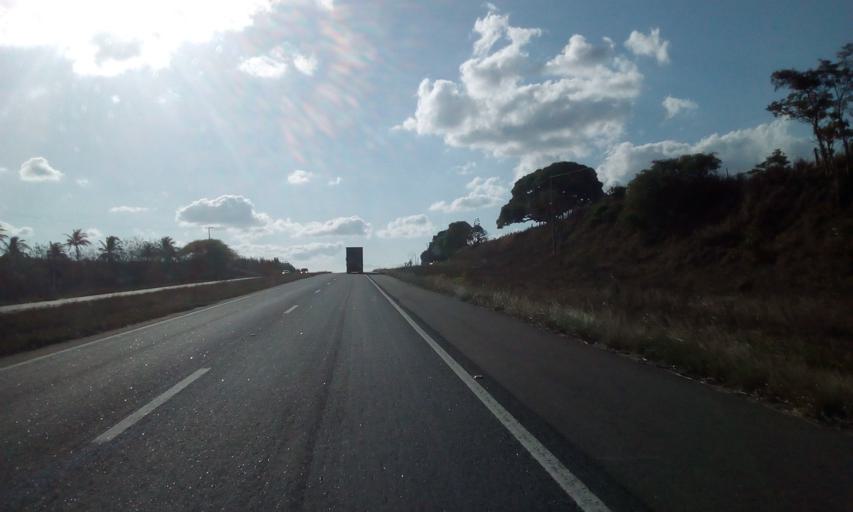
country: BR
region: Paraiba
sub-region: Cruz Do Espirito Santo
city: Cruz do Espirito Santo
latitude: -7.2044
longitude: -35.1322
